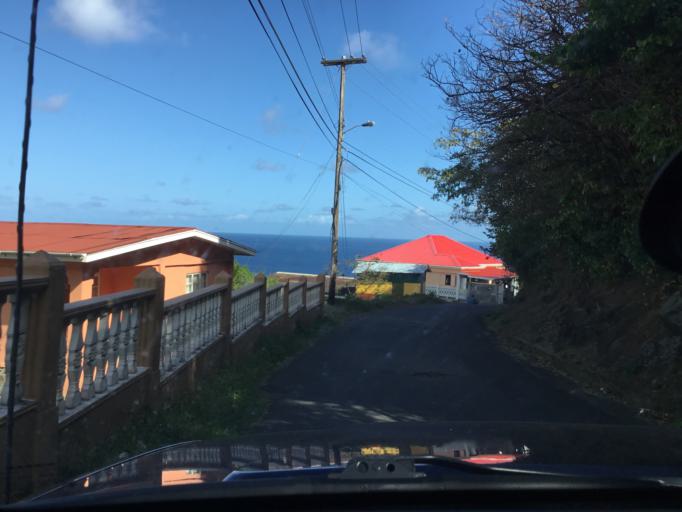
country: VC
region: Charlotte
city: Biabou
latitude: 13.1543
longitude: -61.1562
